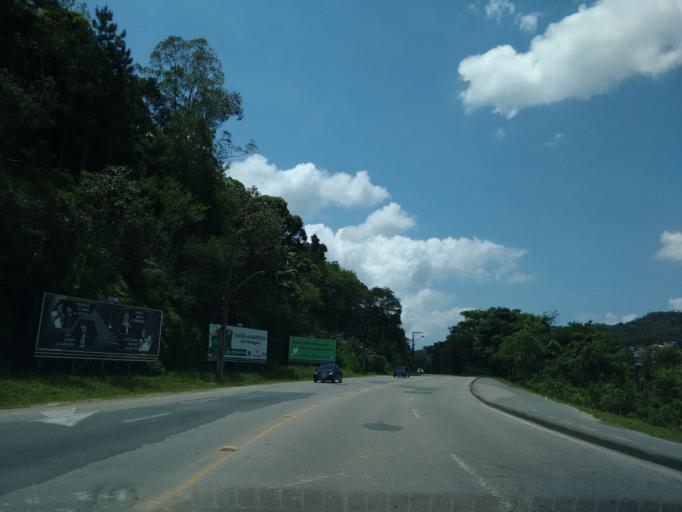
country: BR
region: Santa Catarina
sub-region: Blumenau
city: Blumenau
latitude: -26.9112
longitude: -49.0563
